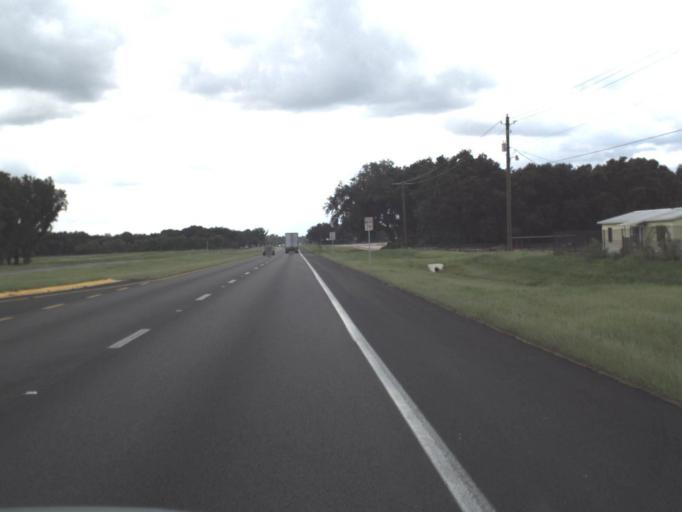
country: US
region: Florida
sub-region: Hillsborough County
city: Plant City
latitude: 28.0638
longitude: -82.1360
